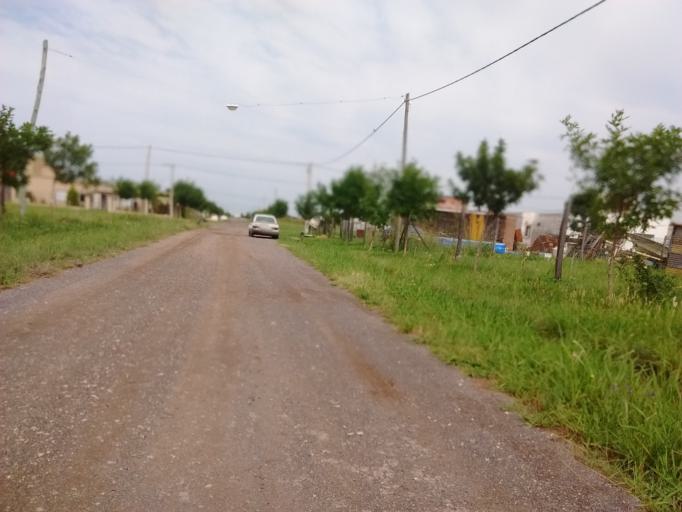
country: AR
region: Santa Fe
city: Funes
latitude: -32.9004
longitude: -60.7996
